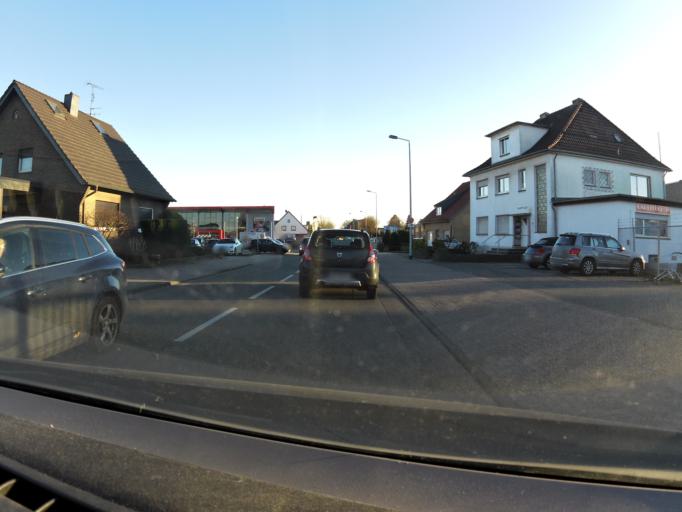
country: NL
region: Limburg
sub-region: Gemeente Venlo
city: Venlo
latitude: 51.3275
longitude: 6.1975
